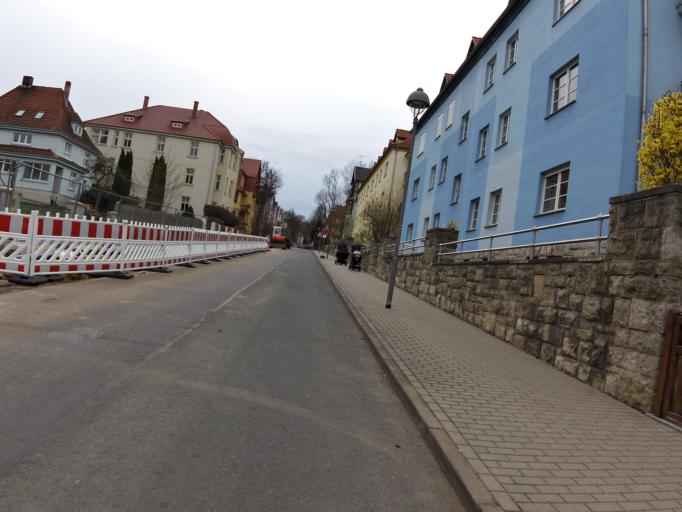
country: DE
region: Thuringia
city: Gotha
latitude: 50.9471
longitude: 10.7158
